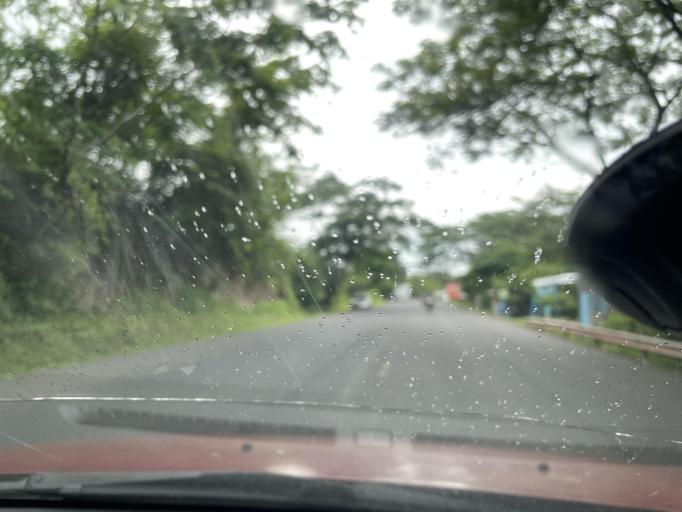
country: SV
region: San Miguel
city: Chirilagua
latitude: 13.3317
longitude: -88.1471
